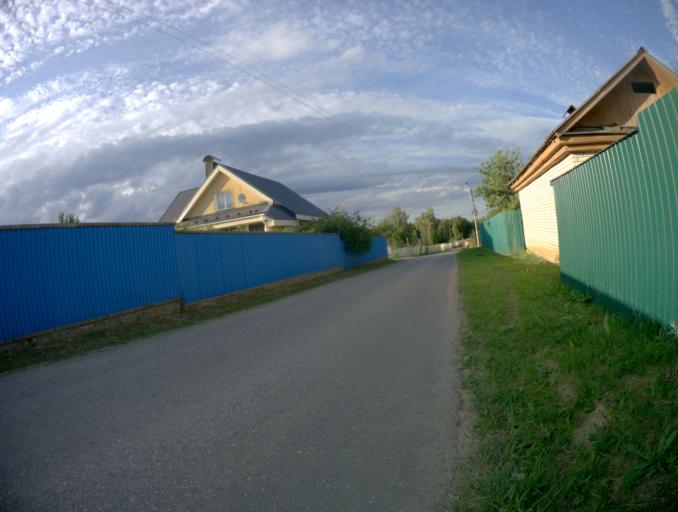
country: RU
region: Vladimir
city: Gorokhovets
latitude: 56.1931
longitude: 42.6742
